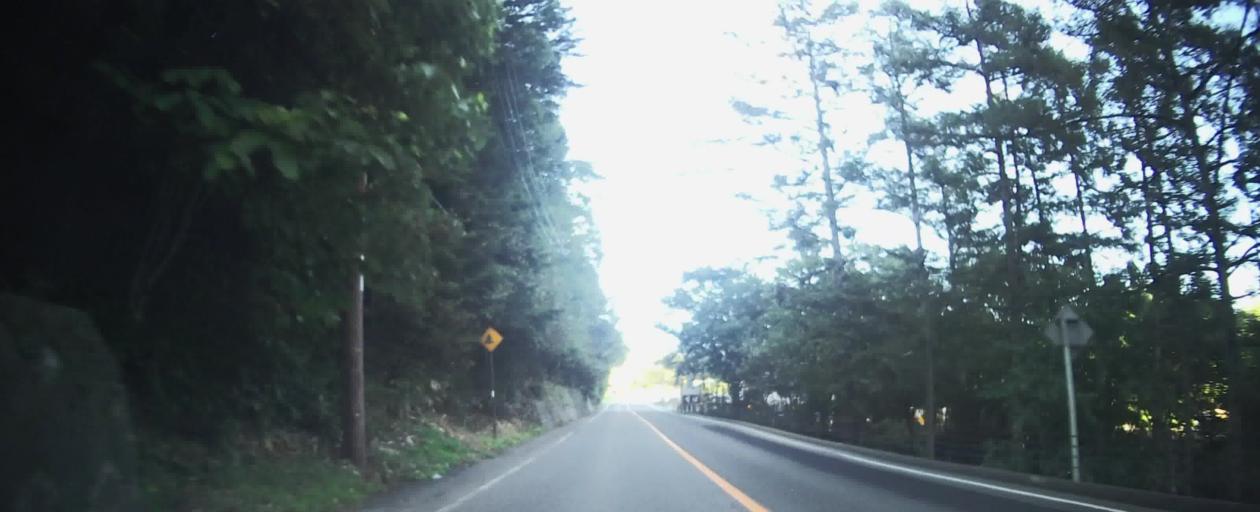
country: JP
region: Nagano
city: Nakano
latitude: 36.6247
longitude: 138.5853
